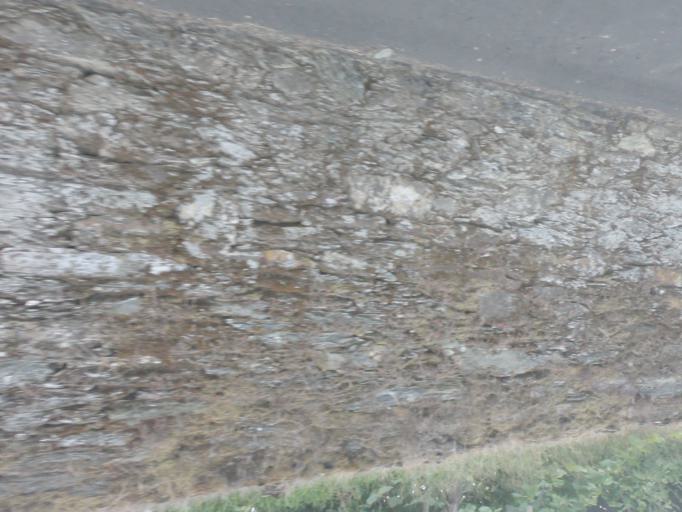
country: PT
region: Vila Real
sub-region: Sabrosa
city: Vilela
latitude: 41.2011
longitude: -7.5327
